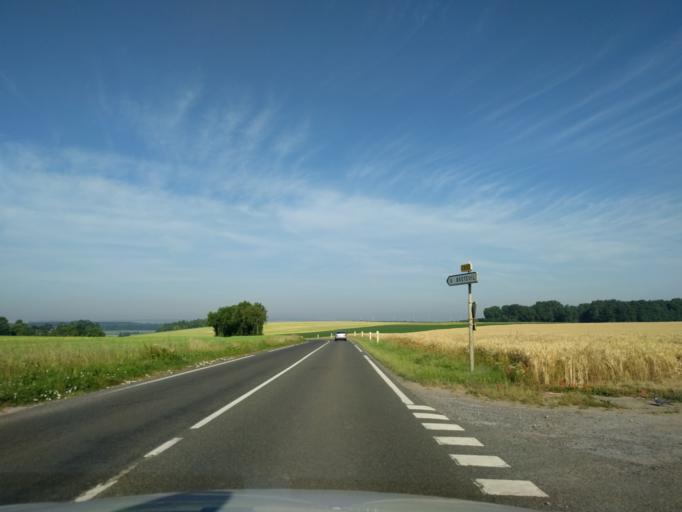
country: FR
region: Picardie
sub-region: Departement de l'Oise
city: Ansauvillers
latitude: 49.6314
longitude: 2.3993
